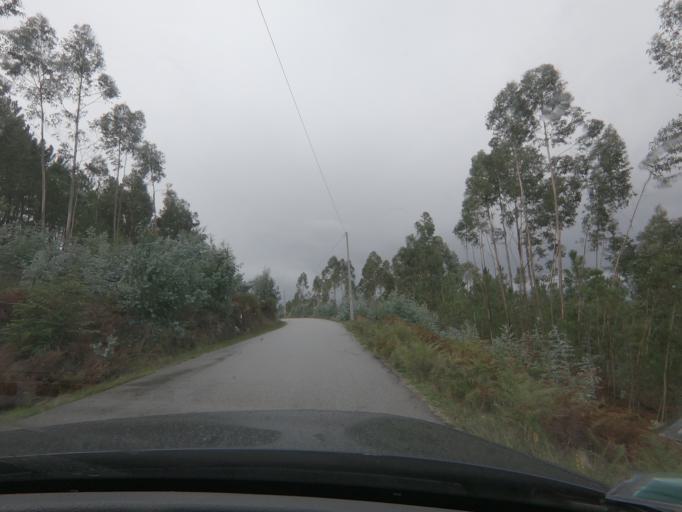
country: PT
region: Vila Real
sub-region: Mondim de Basto
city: Mondim de Basto
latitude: 41.3718
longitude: -7.9392
